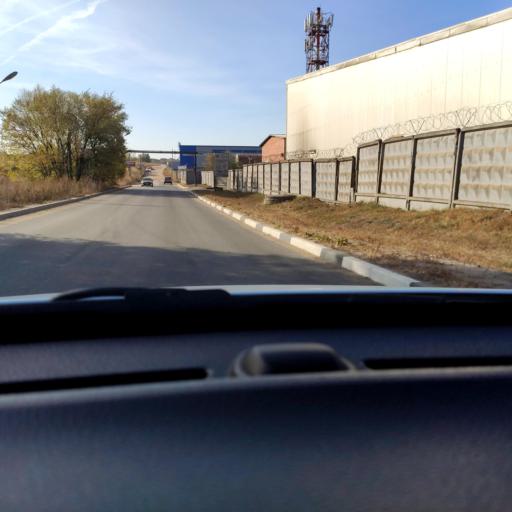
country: RU
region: Voronezj
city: Pridonskoy
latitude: 51.6403
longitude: 39.1106
